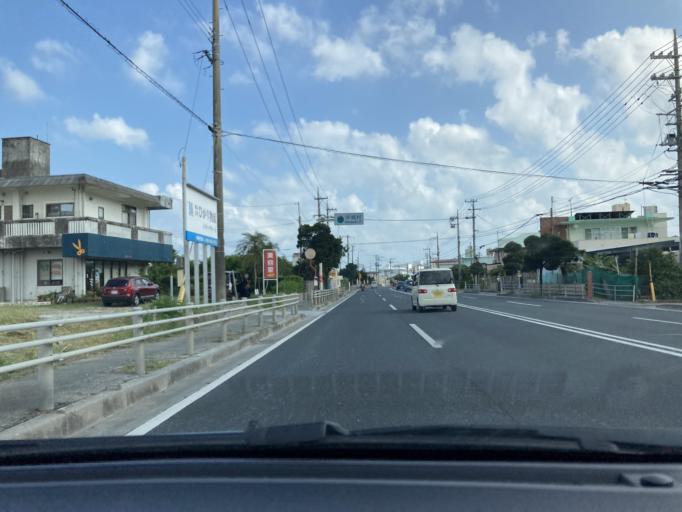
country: JP
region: Okinawa
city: Chatan
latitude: 26.2896
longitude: 127.8129
